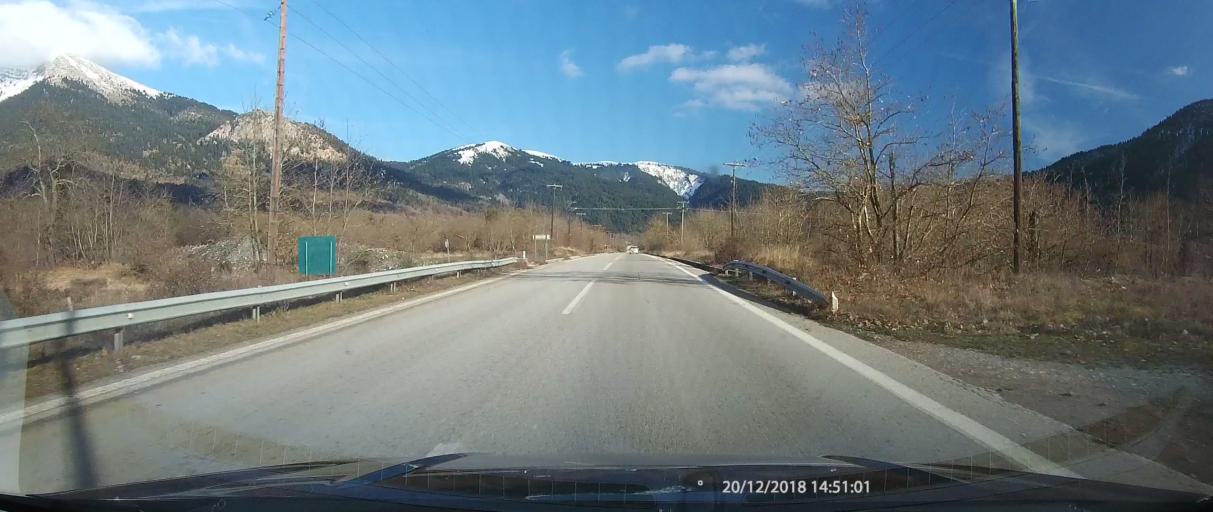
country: GR
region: Central Greece
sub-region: Nomos Evrytanias
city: Karpenisi
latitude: 38.9074
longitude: 21.8351
